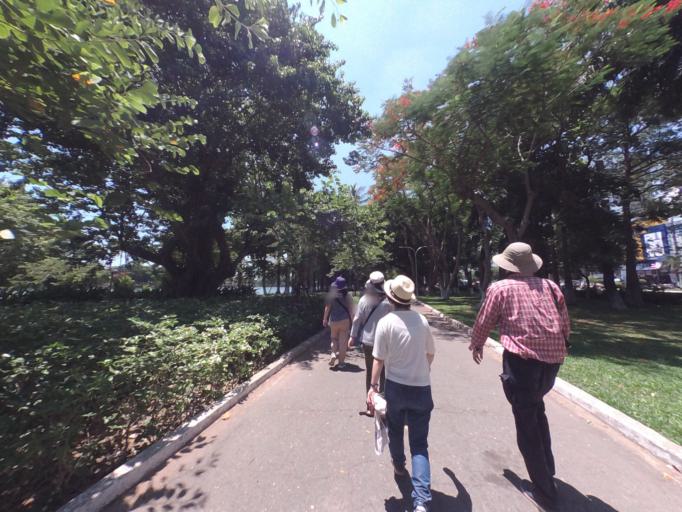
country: VN
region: Da Nang
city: Thanh Khe
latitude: 16.0621
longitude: 108.2048
